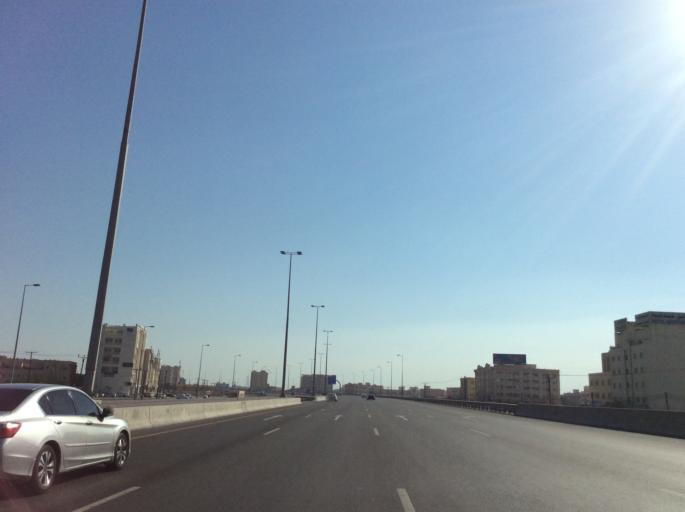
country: OM
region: Al Batinah
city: Al Liwa'
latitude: 24.4349
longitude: 56.6071
